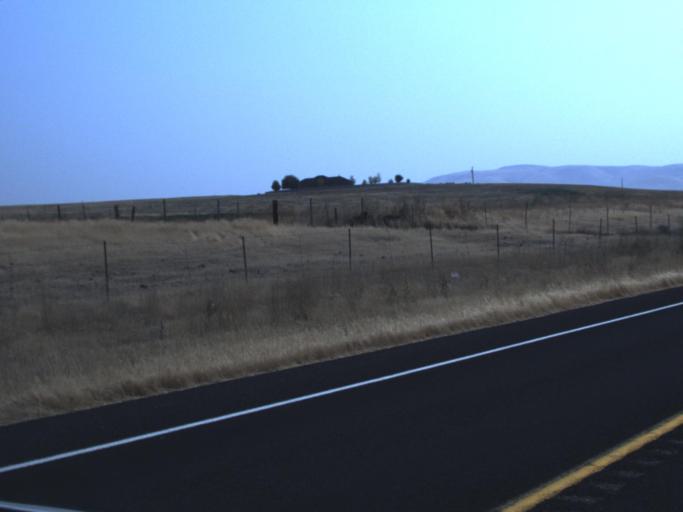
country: US
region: Washington
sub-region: Yakima County
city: Zillah
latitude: 46.5164
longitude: -120.2043
